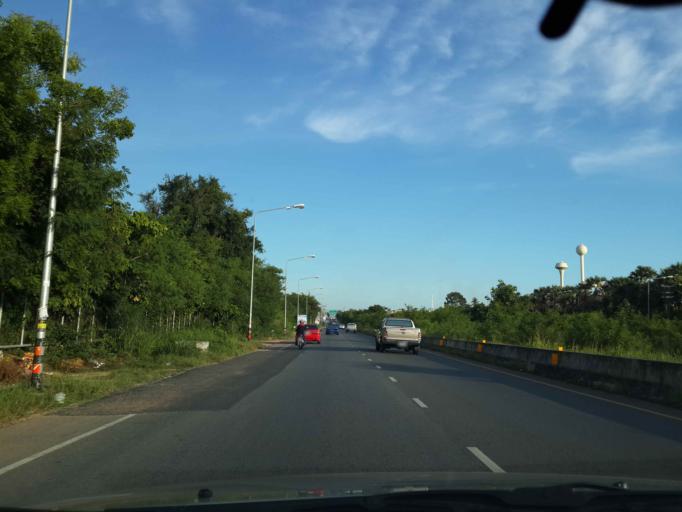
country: TH
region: Chon Buri
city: Phatthaya
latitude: 12.8880
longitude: 100.9022
